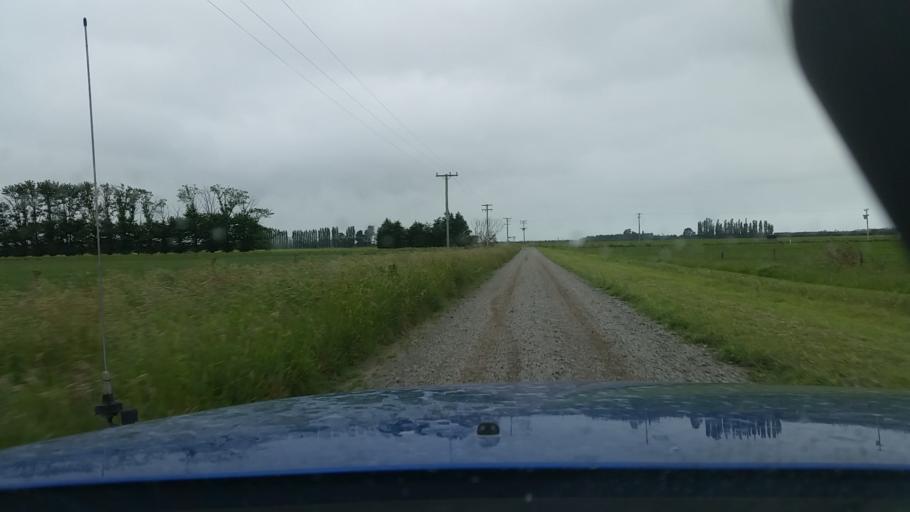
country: NZ
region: Canterbury
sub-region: Ashburton District
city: Tinwald
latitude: -44.0456
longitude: 171.6606
